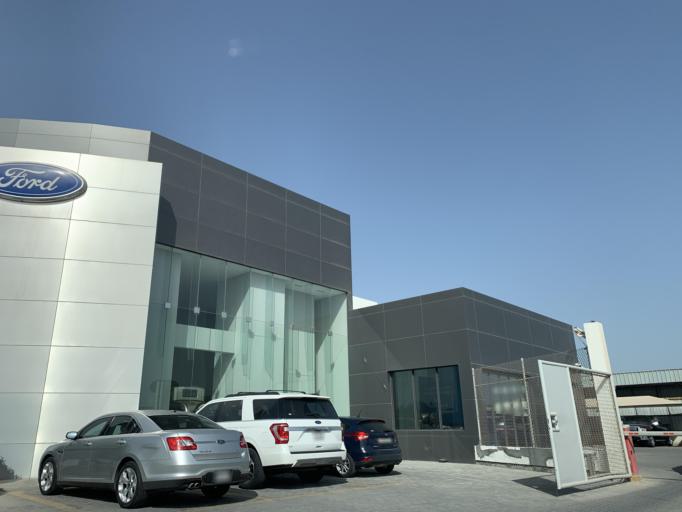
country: BH
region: Northern
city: Sitrah
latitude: 26.1467
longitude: 50.6181
